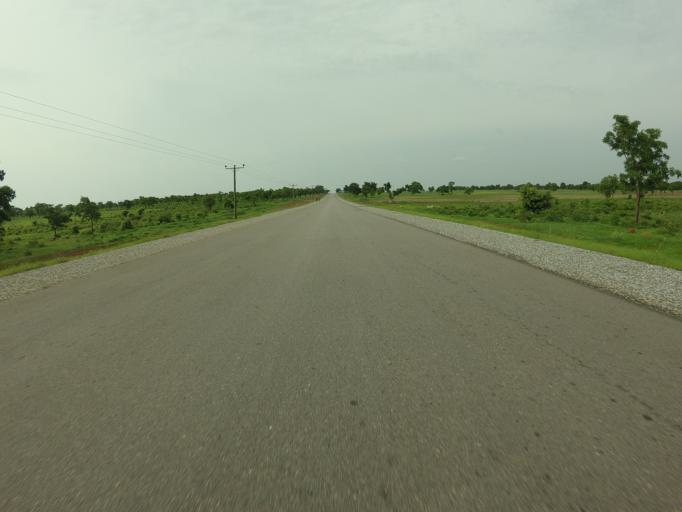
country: GH
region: Northern
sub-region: Yendi
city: Yendi
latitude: 9.8184
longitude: -0.1176
